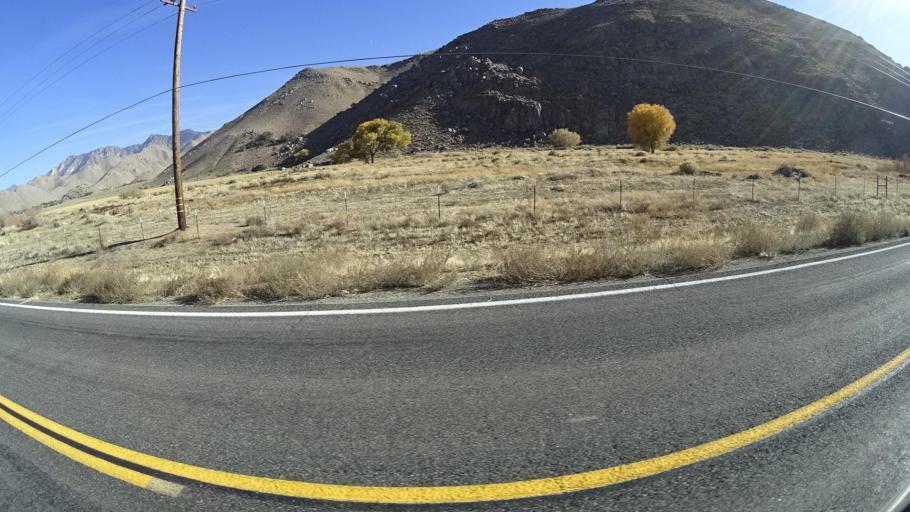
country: US
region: California
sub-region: Kern County
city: Weldon
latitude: 35.6830
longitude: -118.2476
